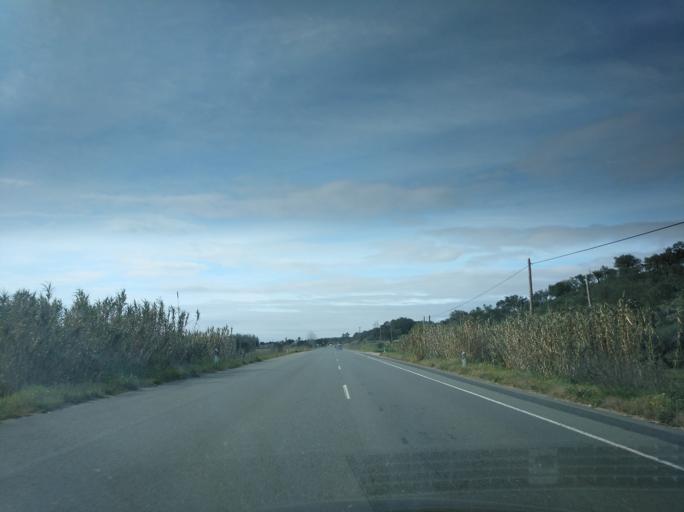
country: PT
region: Setubal
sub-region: Grandola
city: Grandola
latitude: 38.1277
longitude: -8.4645
